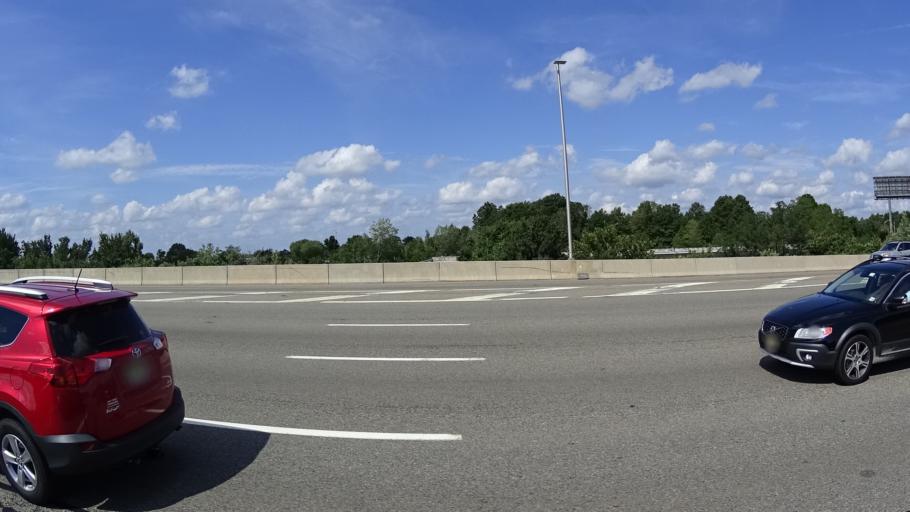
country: US
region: New Jersey
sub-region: Middlesex County
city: Fords
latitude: 40.5181
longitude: -74.3013
